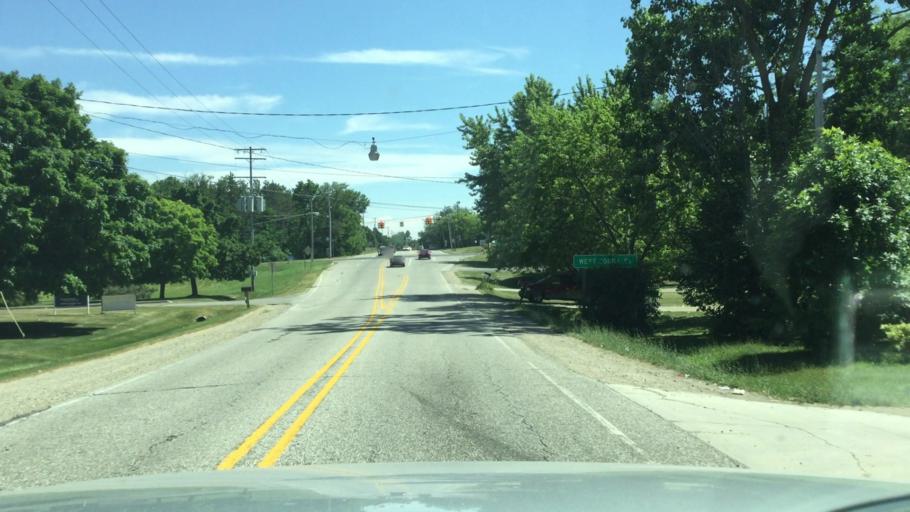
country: US
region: Michigan
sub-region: Genesee County
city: Flint
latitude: 43.0084
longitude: -83.7531
